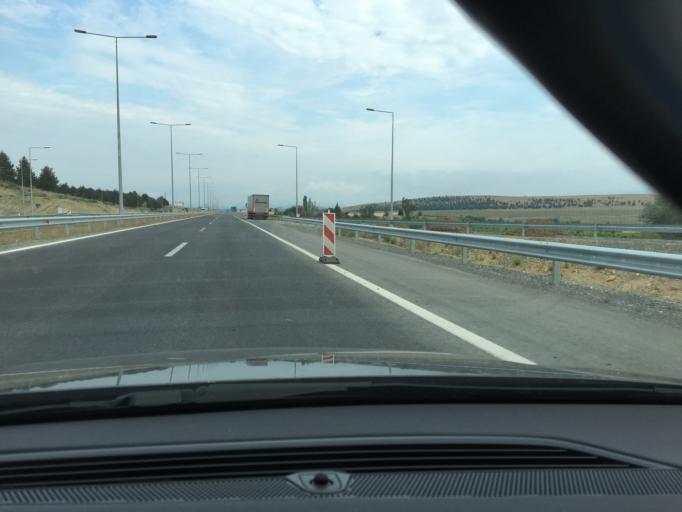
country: MK
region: Stip
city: Shtip
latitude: 41.7826
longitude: 22.1243
